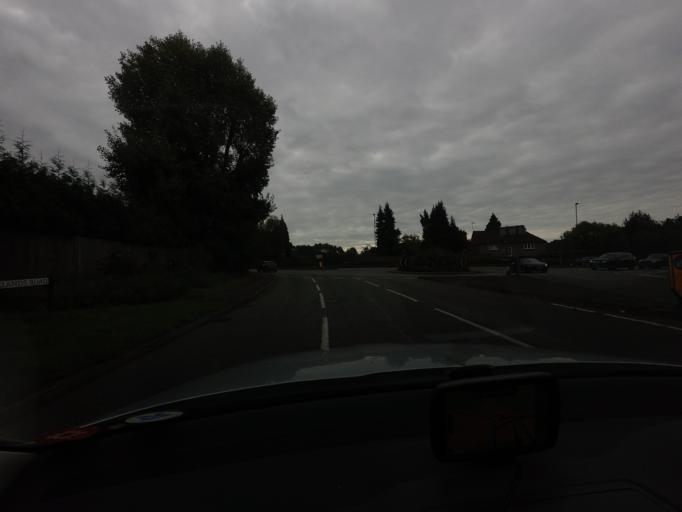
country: GB
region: England
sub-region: Surrey
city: Byfleet
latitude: 51.3415
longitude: -0.4626
